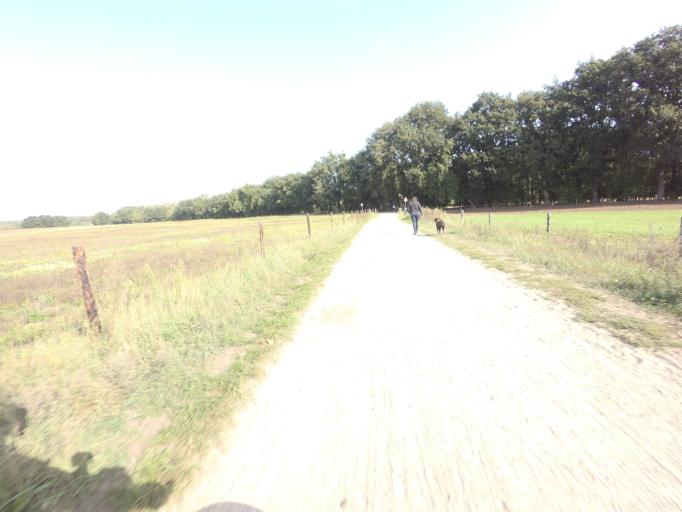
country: NL
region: Limburg
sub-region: Gemeente Roerdalen
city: Herkenbosch
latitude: 51.1686
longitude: 6.0850
